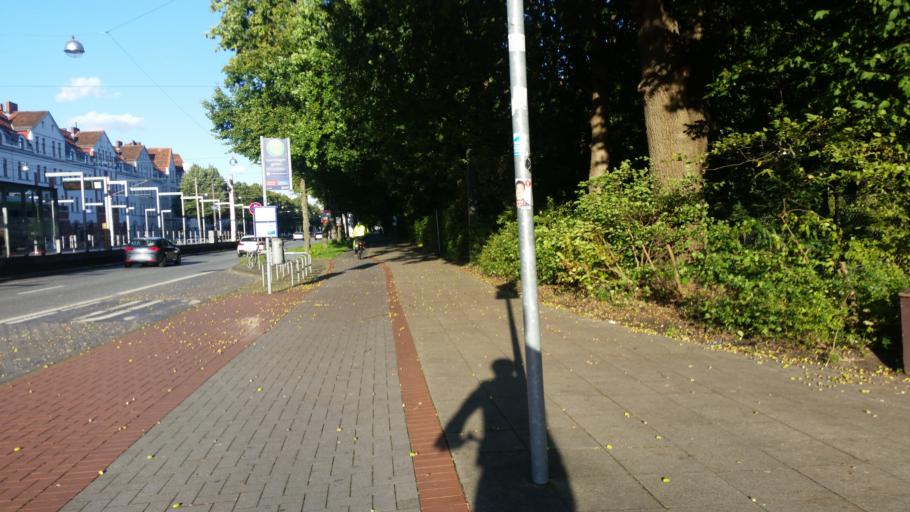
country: DE
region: Lower Saxony
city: Hannover
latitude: 52.4001
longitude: 9.7816
